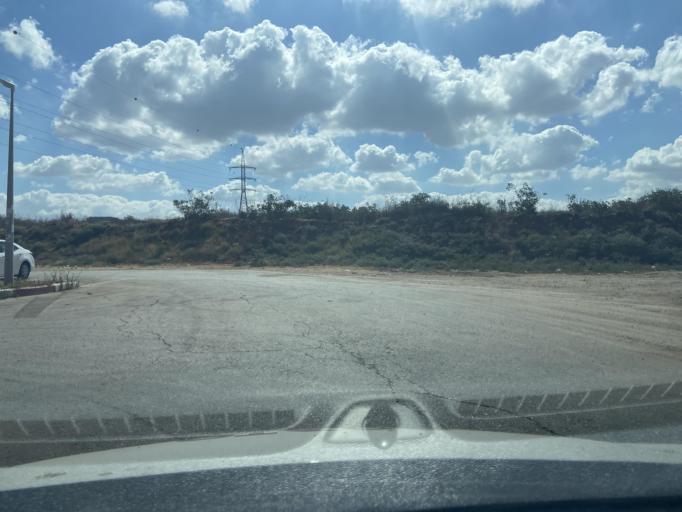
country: IL
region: Central District
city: Yehud
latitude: 32.0239
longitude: 34.8923
